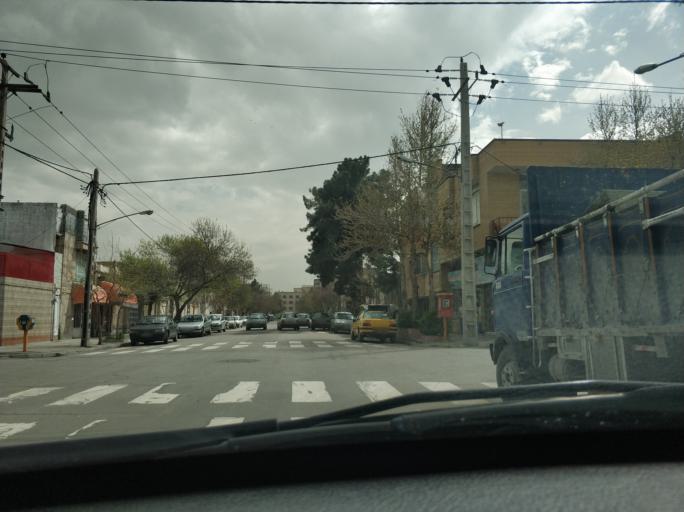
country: IR
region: Razavi Khorasan
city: Mashhad
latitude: 36.2741
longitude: 59.5729
